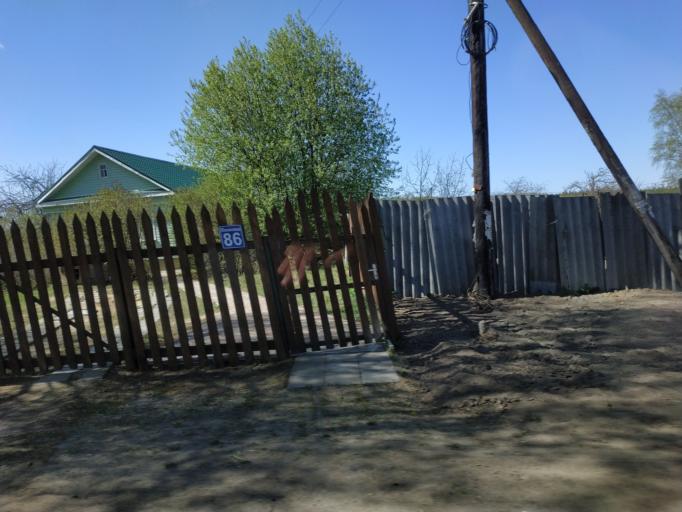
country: RU
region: Moskovskaya
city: Malyshevo
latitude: 55.4742
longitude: 38.3949
